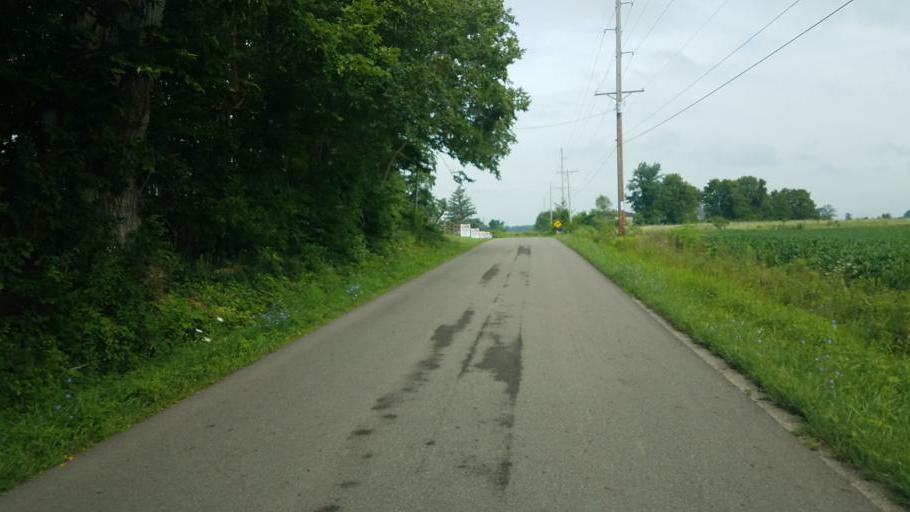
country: US
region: Ohio
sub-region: Delaware County
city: Ashley
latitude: 40.3651
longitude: -82.9056
